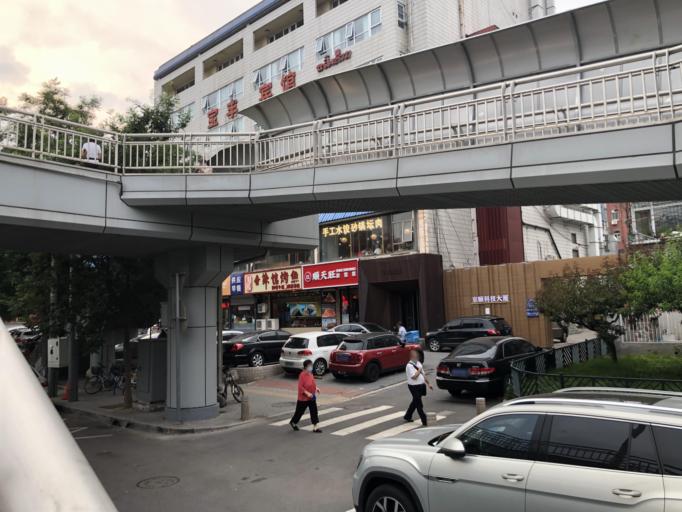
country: CN
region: Beijing
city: Sijiqing
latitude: 39.9313
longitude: 116.3094
